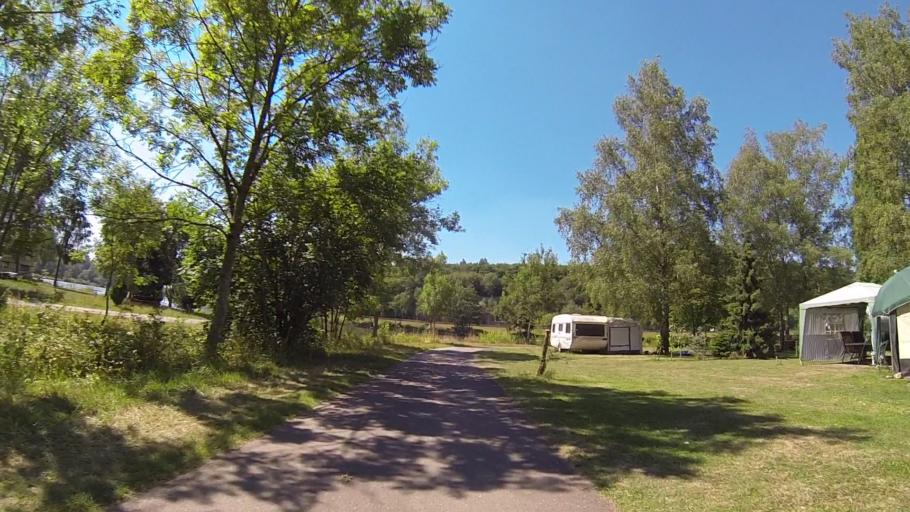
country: DE
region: Rheinland-Pfalz
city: Palzem
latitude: 49.5594
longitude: 6.3822
